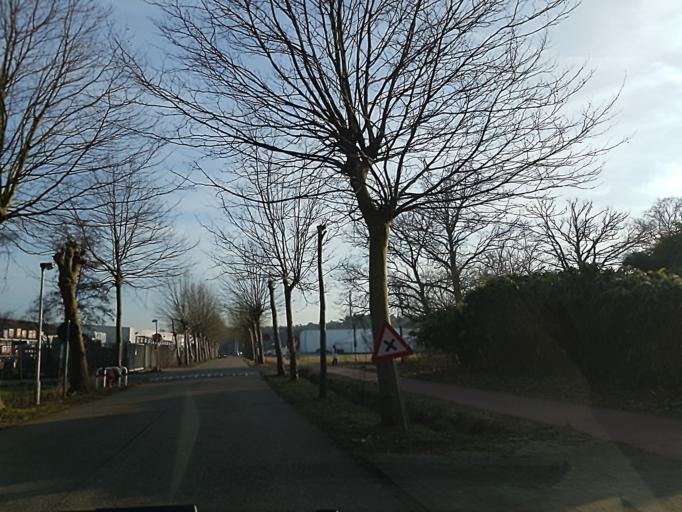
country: BE
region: Flanders
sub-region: Provincie Antwerpen
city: Schilde
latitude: 51.2514
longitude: 4.6035
